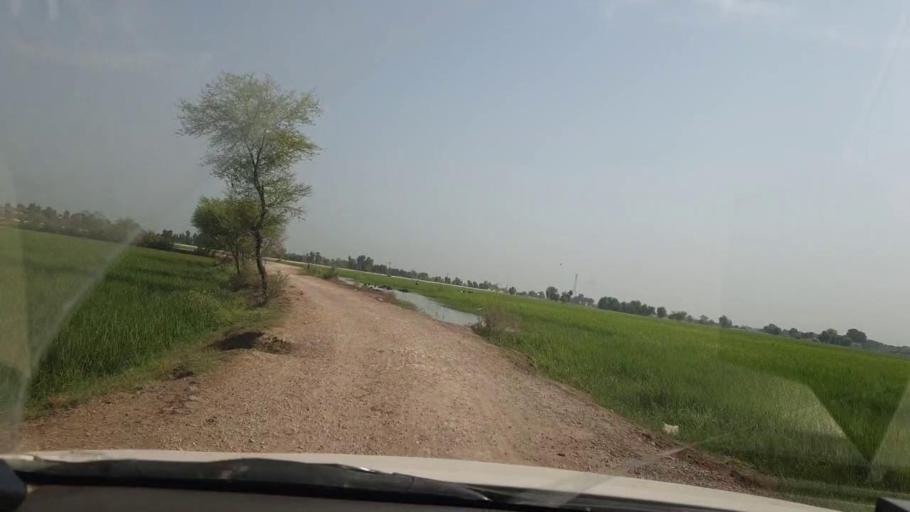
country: PK
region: Sindh
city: Chak
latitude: 27.8394
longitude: 68.7994
